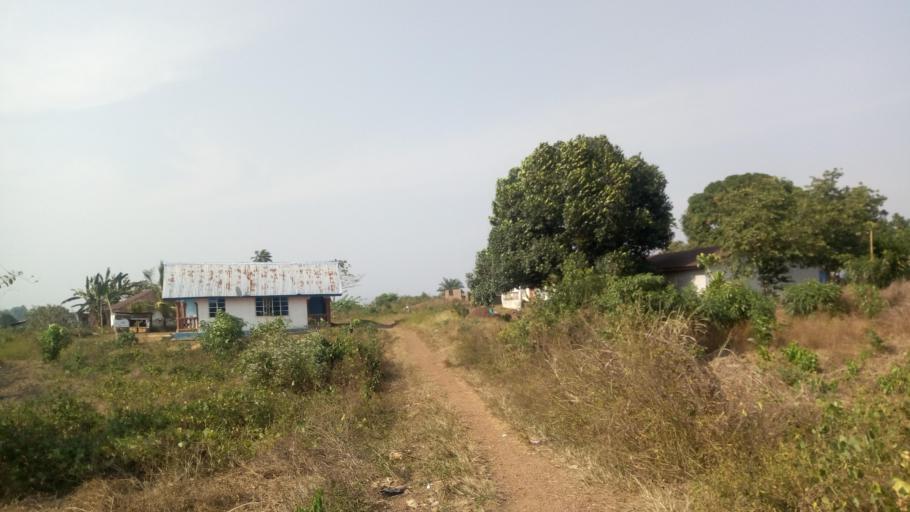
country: SL
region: Southern Province
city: Mogbwemo
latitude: 7.6180
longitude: -12.1807
